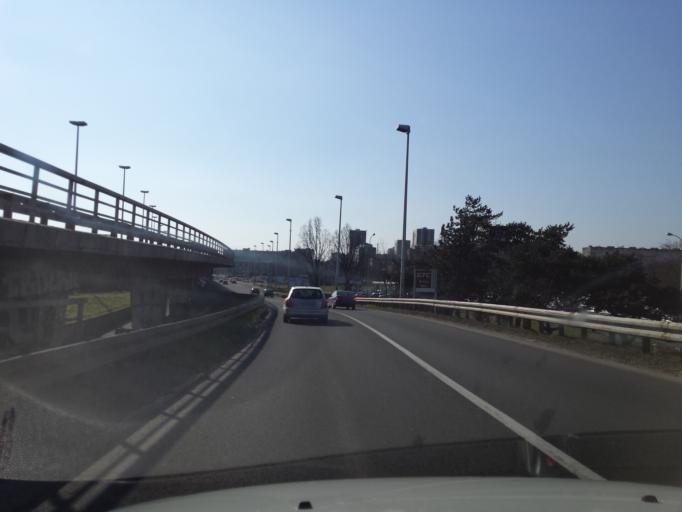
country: HR
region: Grad Zagreb
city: Novi Zagreb
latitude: 45.7811
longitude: 16.0009
